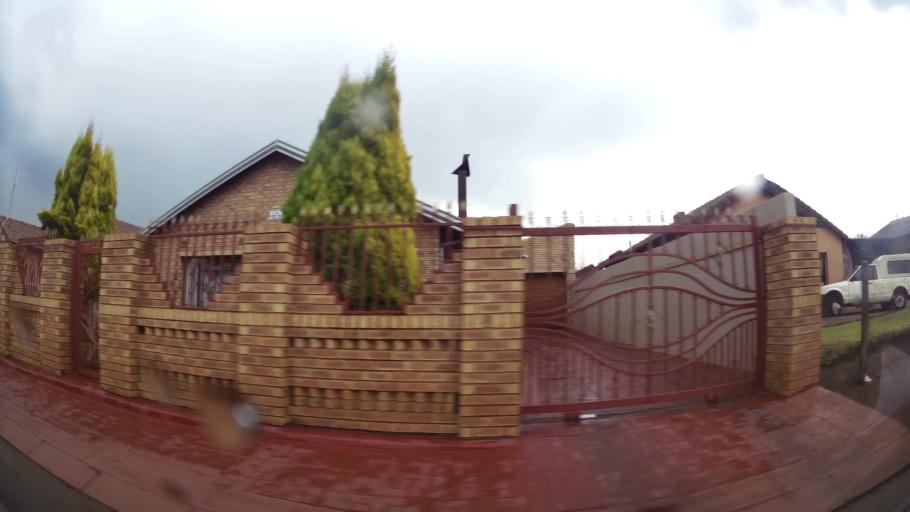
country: ZA
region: Gauteng
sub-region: Ekurhuleni Metropolitan Municipality
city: Germiston
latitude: -26.3680
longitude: 28.1357
